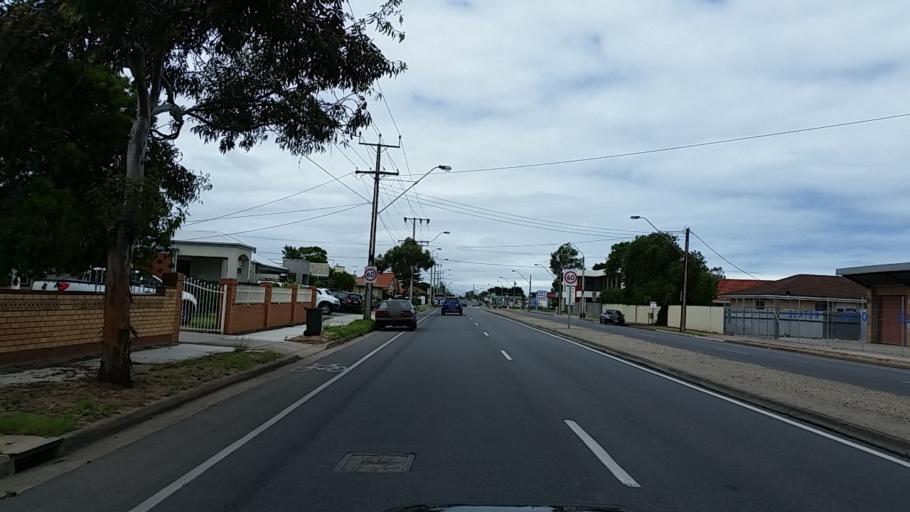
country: AU
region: South Australia
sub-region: Charles Sturt
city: Seaton
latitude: -34.8988
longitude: 138.5142
